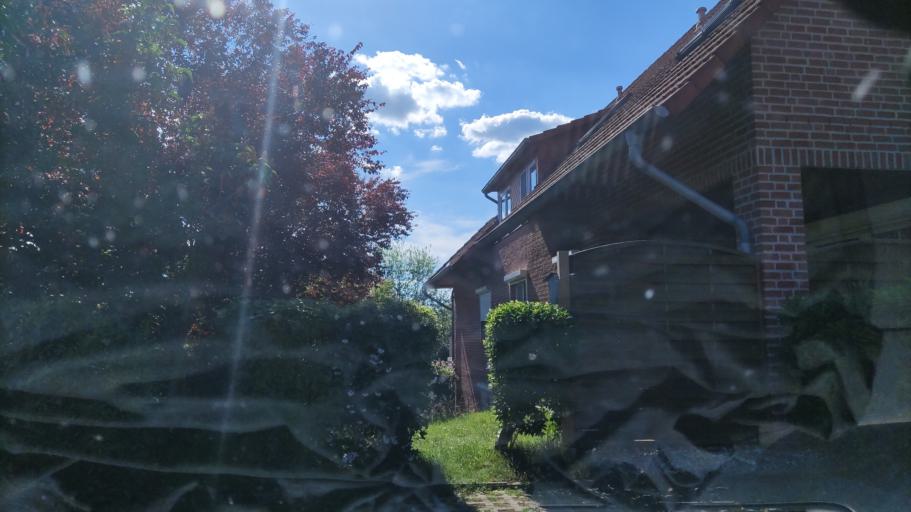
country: DE
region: Lower Saxony
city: Melbeck
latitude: 53.1750
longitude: 10.4092
